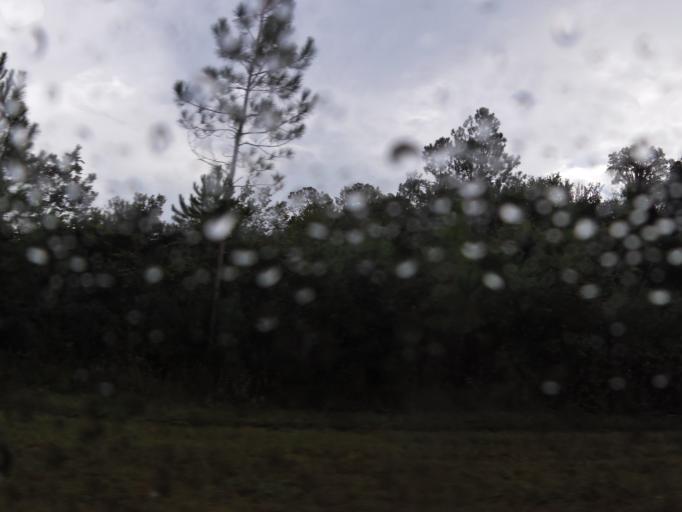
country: US
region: Florida
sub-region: Baker County
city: Macclenny
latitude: 30.4271
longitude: -82.0935
